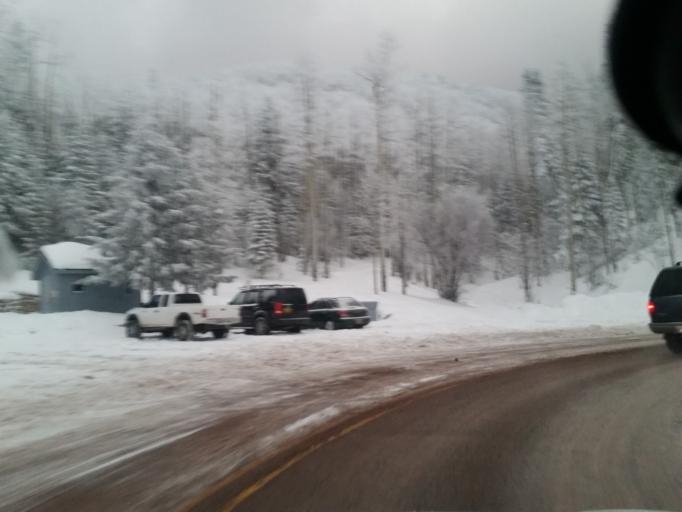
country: US
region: New Mexico
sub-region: Santa Fe County
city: Santa Fe
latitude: 35.7695
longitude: -105.8094
